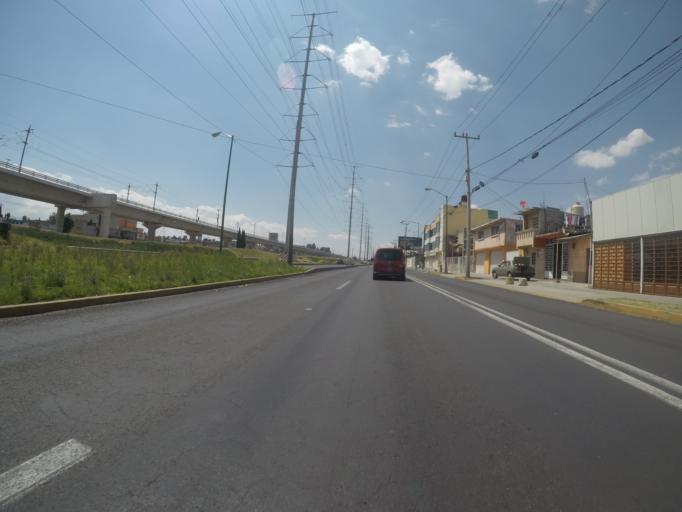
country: MX
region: Mexico
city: San Buenaventura
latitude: 19.2681
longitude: -99.6553
